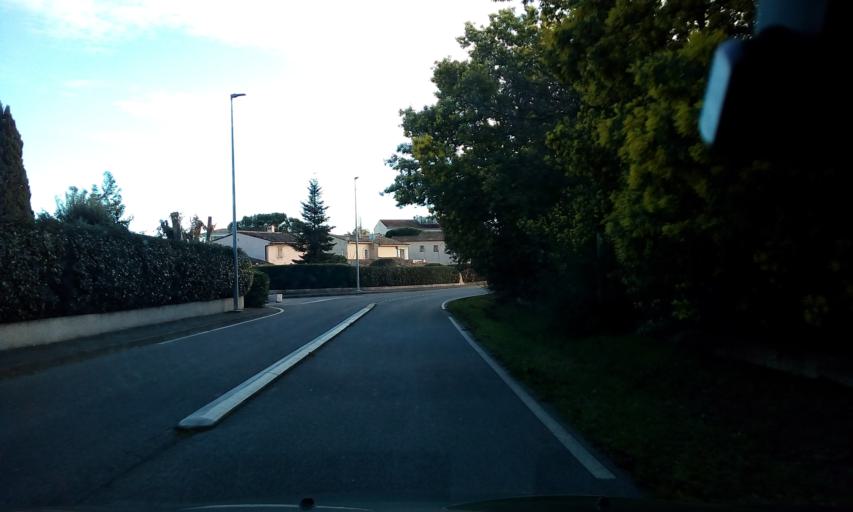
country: FR
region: Provence-Alpes-Cote d'Azur
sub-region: Departement du Var
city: Saint-Raphael
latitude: 43.4383
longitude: 6.7670
